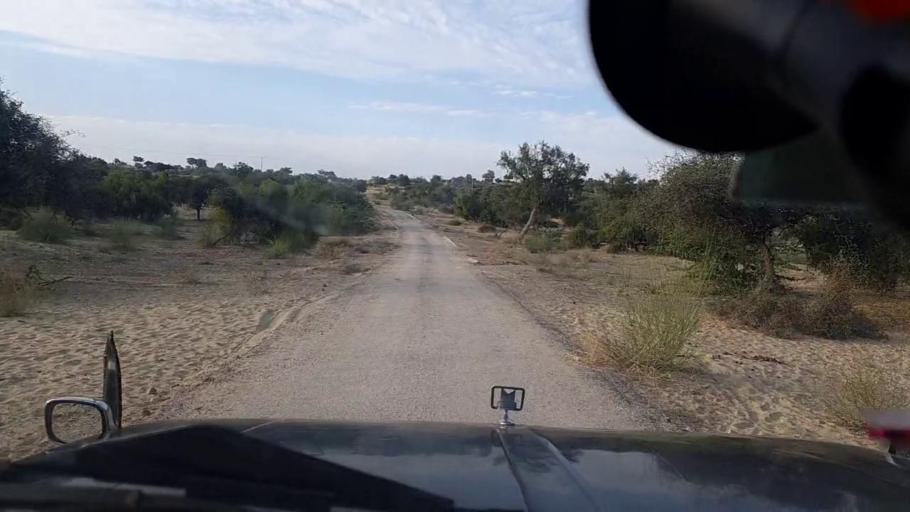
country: PK
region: Sindh
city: Diplo
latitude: 24.4649
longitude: 69.7917
